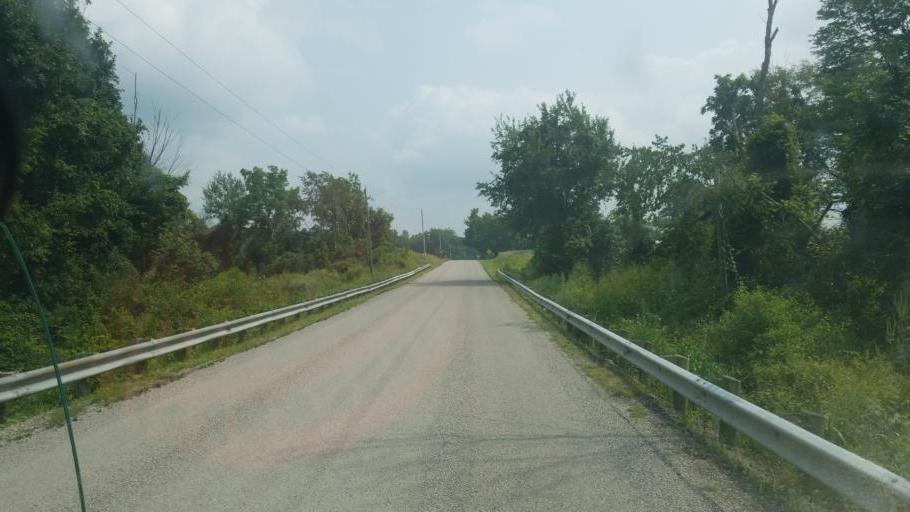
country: US
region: Ohio
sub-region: Huron County
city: Greenwich
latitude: 41.0550
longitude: -82.5229
